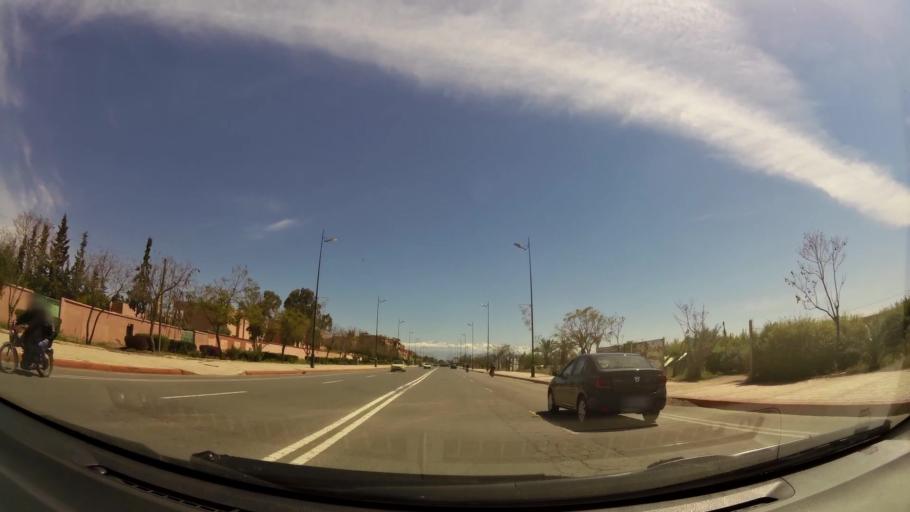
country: MA
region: Marrakech-Tensift-Al Haouz
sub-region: Marrakech
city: Marrakesh
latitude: 31.6092
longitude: -7.9732
